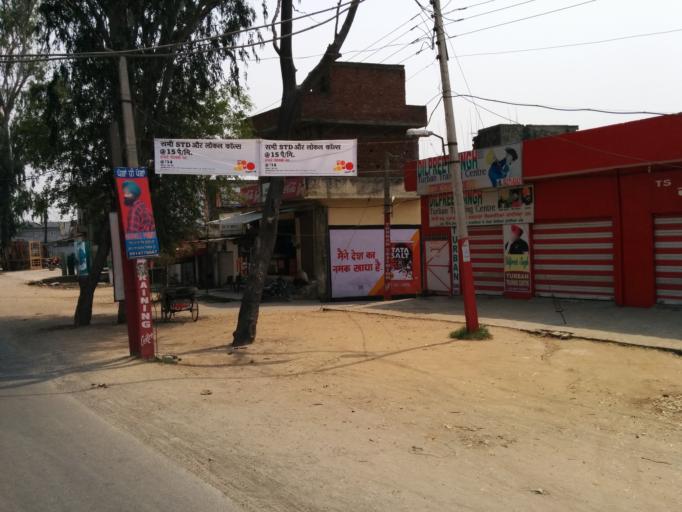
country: IN
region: Punjab
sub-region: Gurdaspur
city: Gurdaspur
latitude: 32.0325
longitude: 75.3984
